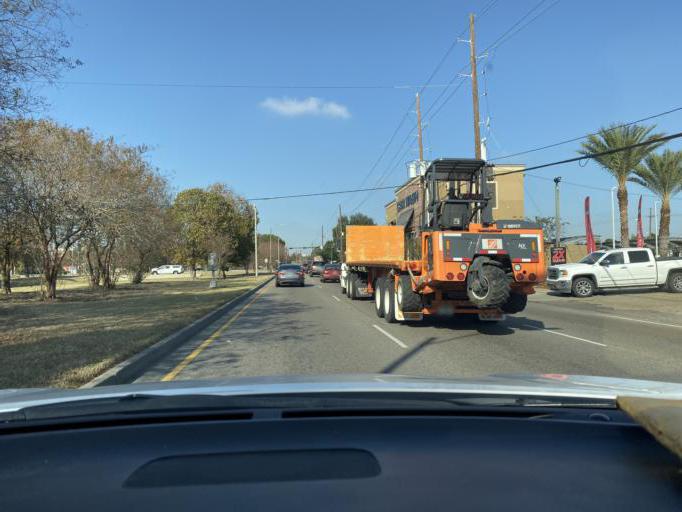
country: US
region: Louisiana
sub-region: Jefferson Parish
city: Terrytown
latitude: 29.9238
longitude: -90.0186
